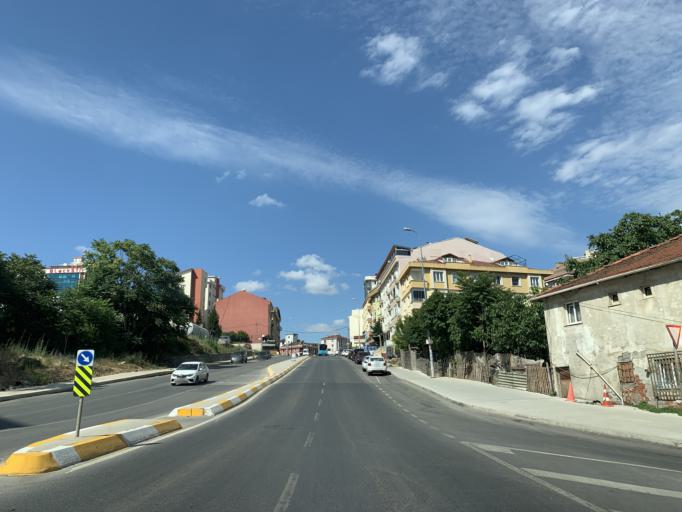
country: TR
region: Istanbul
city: Pendik
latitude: 40.8895
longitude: 29.2647
